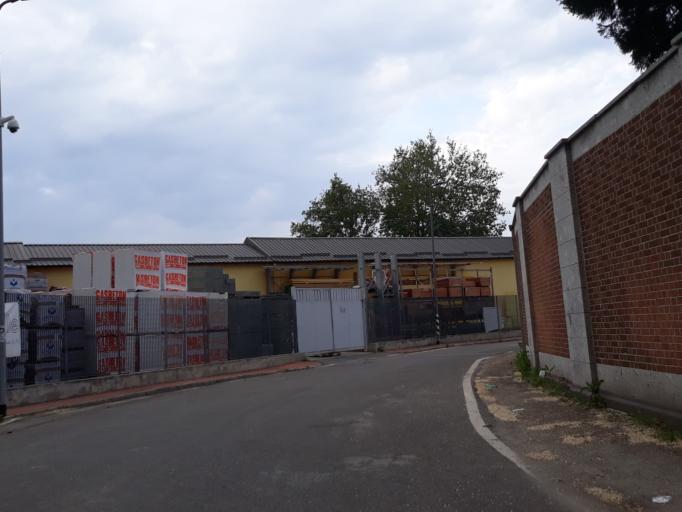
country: IT
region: Lombardy
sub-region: Citta metropolitana di Milano
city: Milano
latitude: 45.4887
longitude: 9.1738
